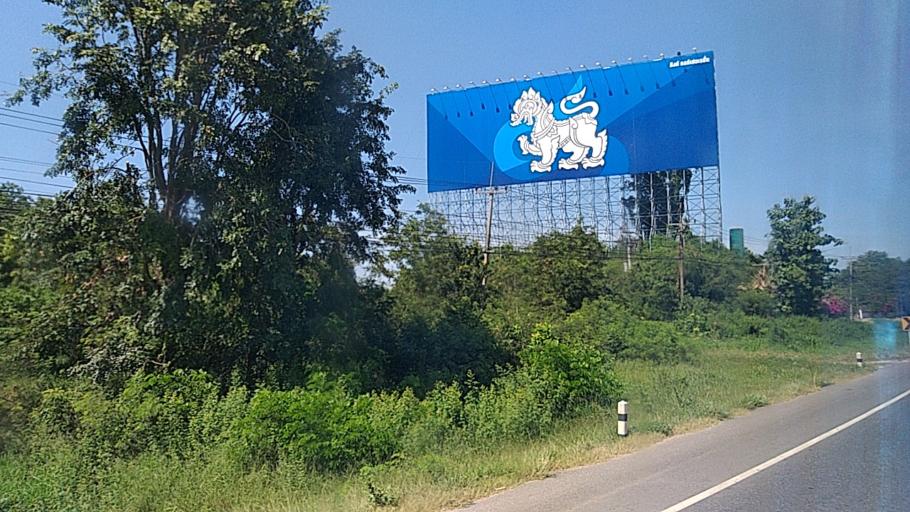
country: TH
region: Khon Kaen
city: Ban Haet
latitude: 16.3026
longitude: 102.7885
